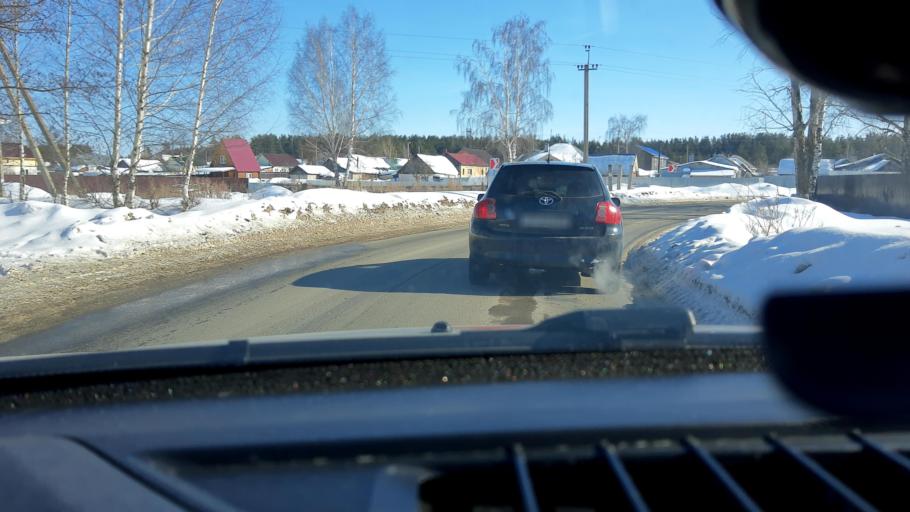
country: RU
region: Nizjnij Novgorod
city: Volodarsk
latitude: 56.2302
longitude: 43.2089
